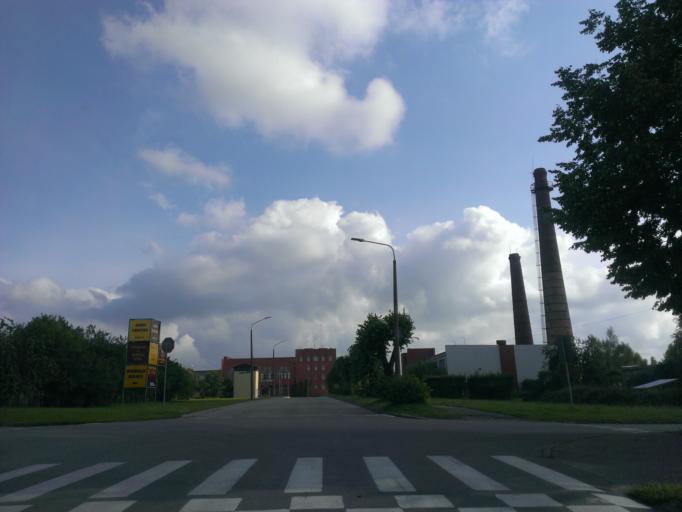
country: LV
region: Priekuli
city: Priekuli
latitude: 57.3097
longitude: 25.3610
